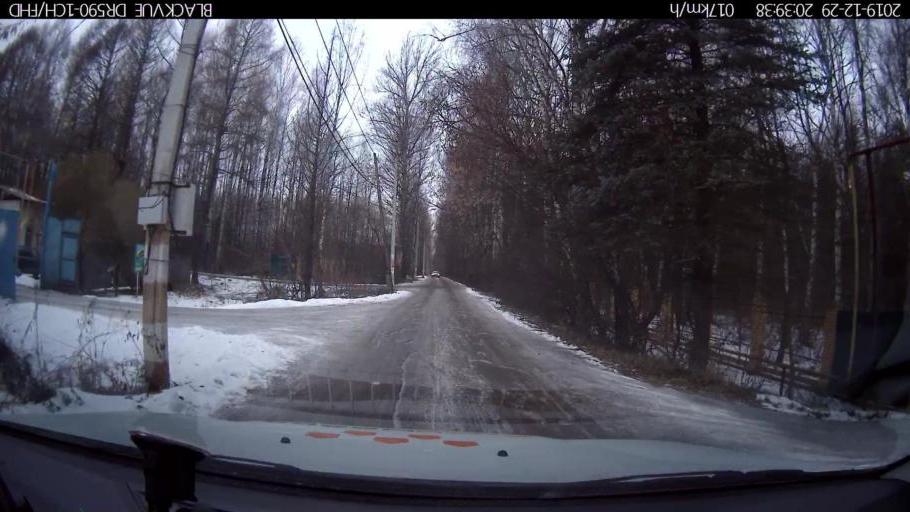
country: RU
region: Nizjnij Novgorod
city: Afonino
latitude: 56.1920
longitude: 44.0478
